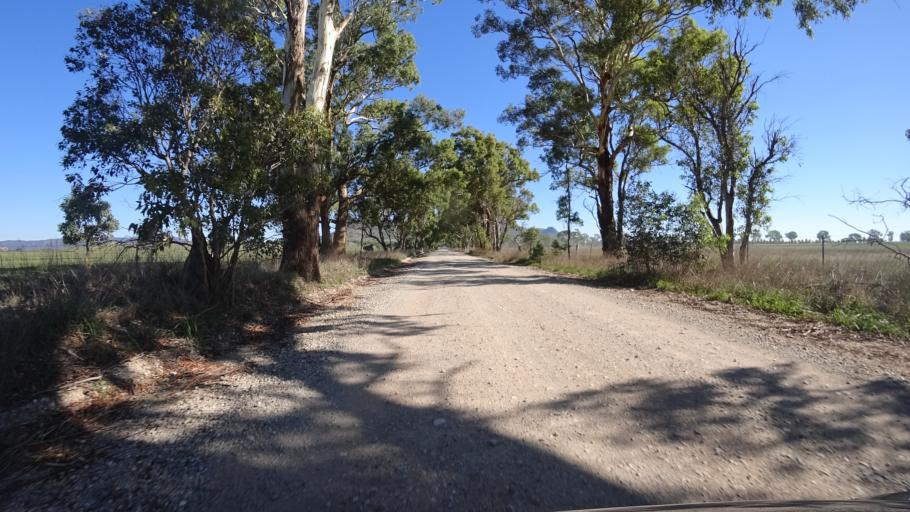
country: AU
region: New South Wales
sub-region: Mid-Western Regional
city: Kandos
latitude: -32.8242
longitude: 150.0210
